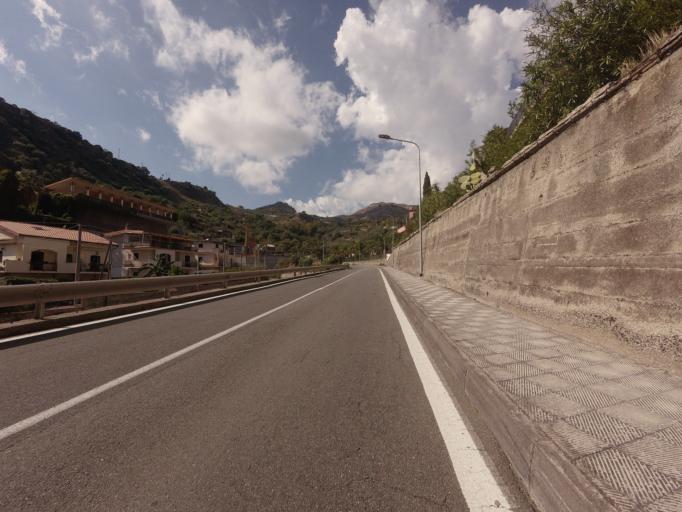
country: IT
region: Sicily
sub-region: Messina
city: Castelmola
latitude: 37.8455
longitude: 15.2785
